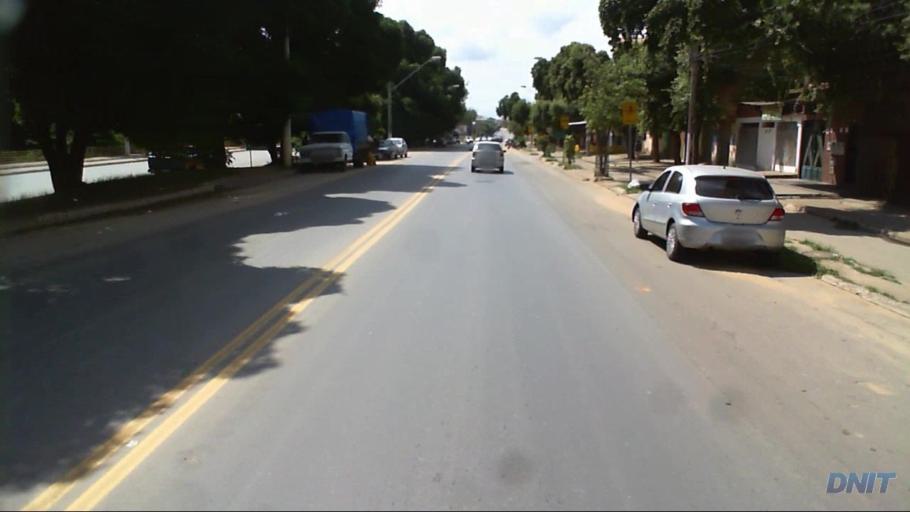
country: BR
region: Minas Gerais
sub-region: Governador Valadares
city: Governador Valadares
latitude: -18.8864
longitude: -41.9703
